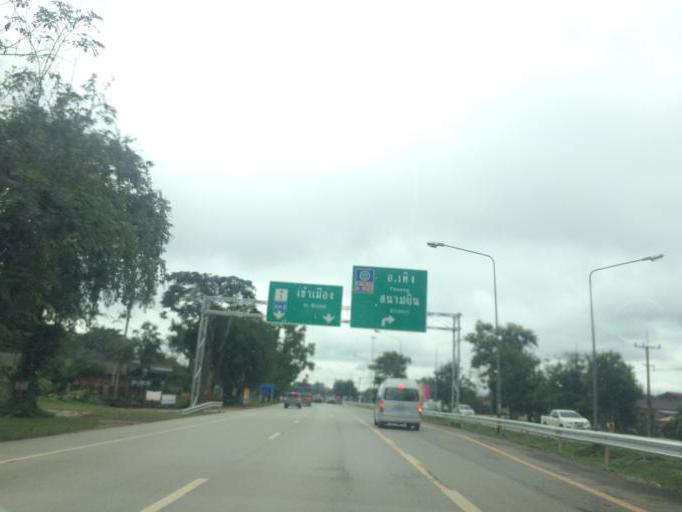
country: TH
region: Chiang Rai
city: Chiang Rai
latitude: 19.8482
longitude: 99.8071
